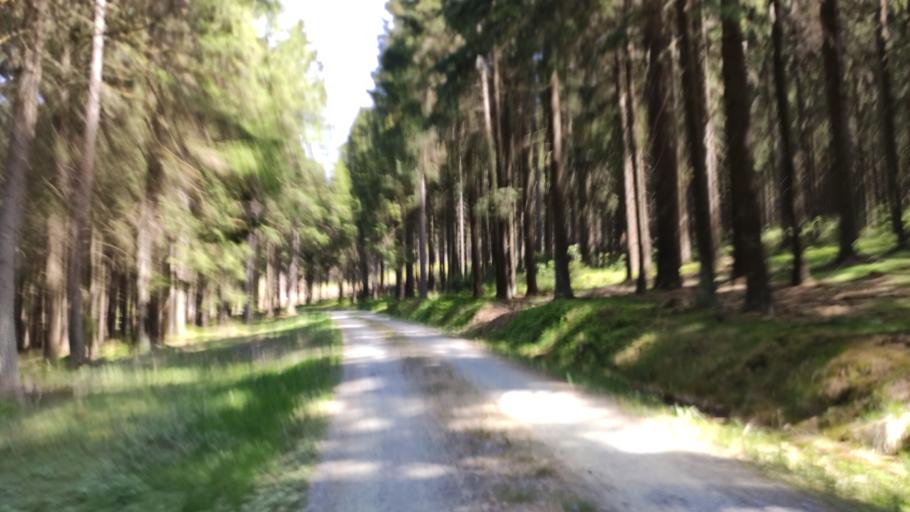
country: DE
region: Bavaria
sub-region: Upper Franconia
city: Reichenbach
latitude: 50.4497
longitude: 11.4478
